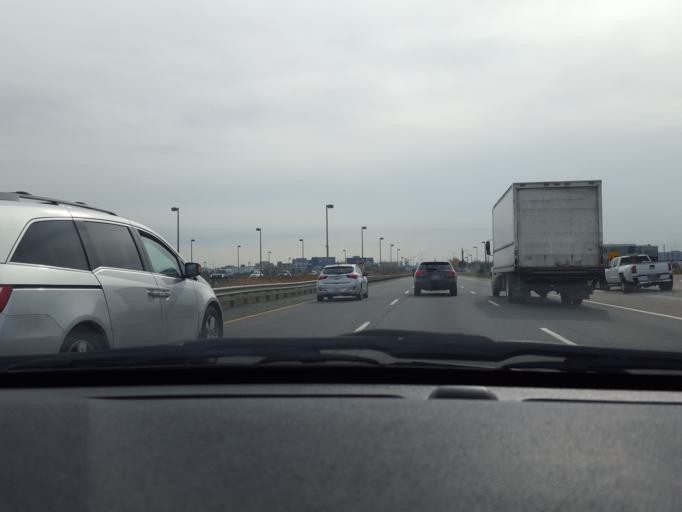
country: CA
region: Ontario
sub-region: York
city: Richmond Hill
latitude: 43.8686
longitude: -79.3764
